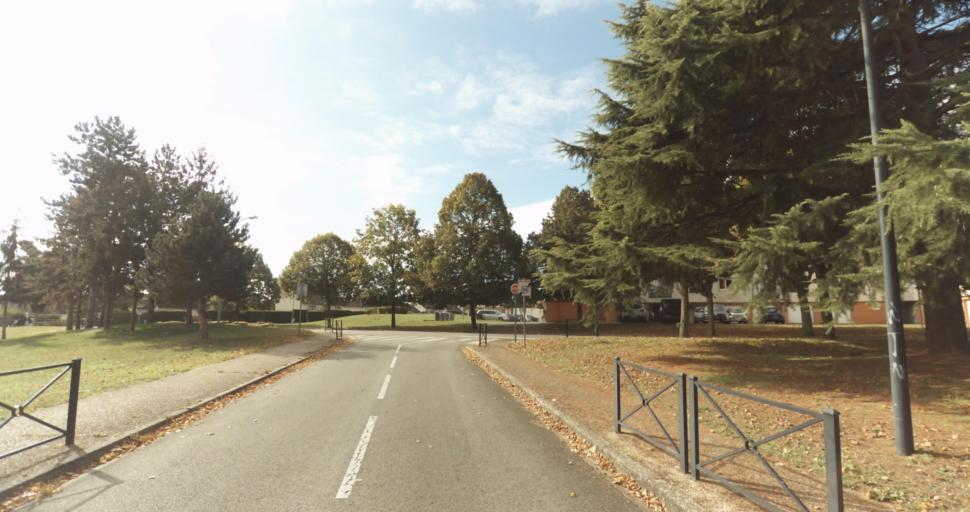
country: FR
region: Centre
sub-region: Departement d'Eure-et-Loir
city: Garnay
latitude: 48.7326
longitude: 1.3380
